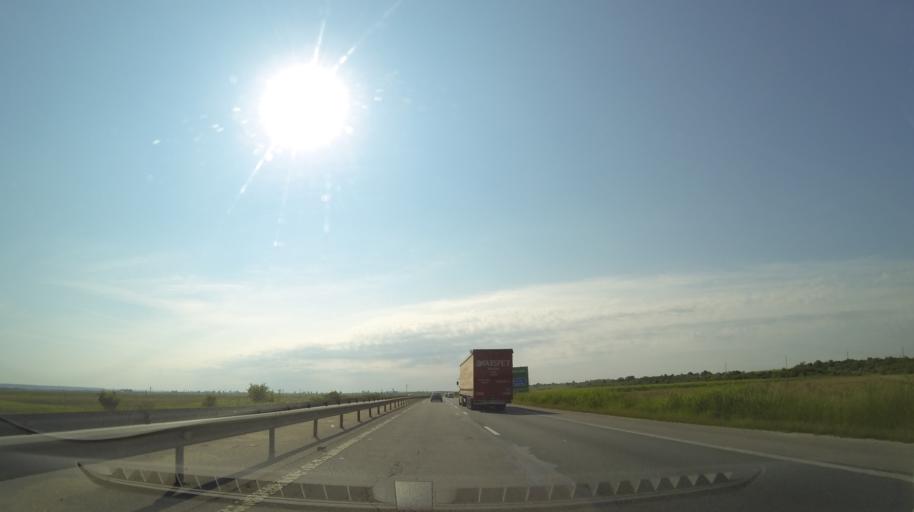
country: RO
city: Oarja Sat
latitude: 44.7740
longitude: 25.0184
